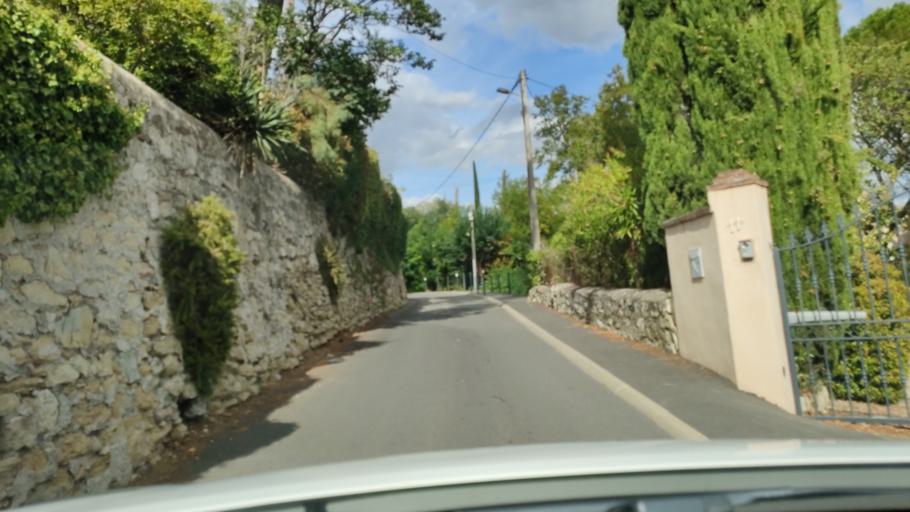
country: FR
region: Languedoc-Roussillon
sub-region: Departement du Gard
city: Villeneuve-les-Avignon
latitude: 43.9578
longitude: 4.7905
